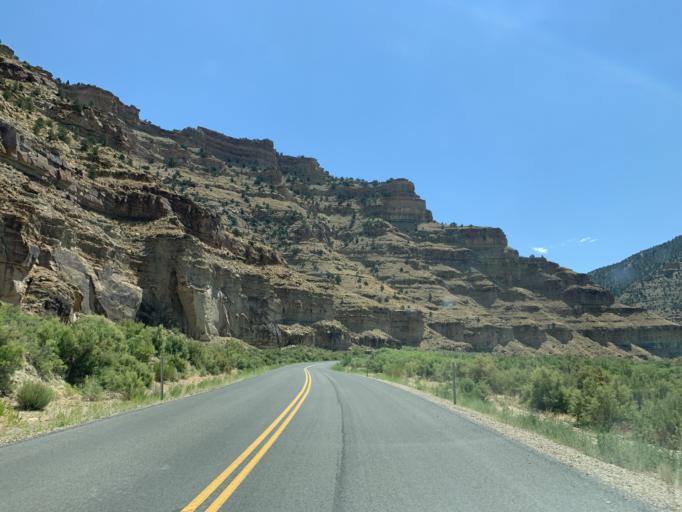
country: US
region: Utah
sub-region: Carbon County
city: East Carbon City
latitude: 39.8127
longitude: -110.2761
